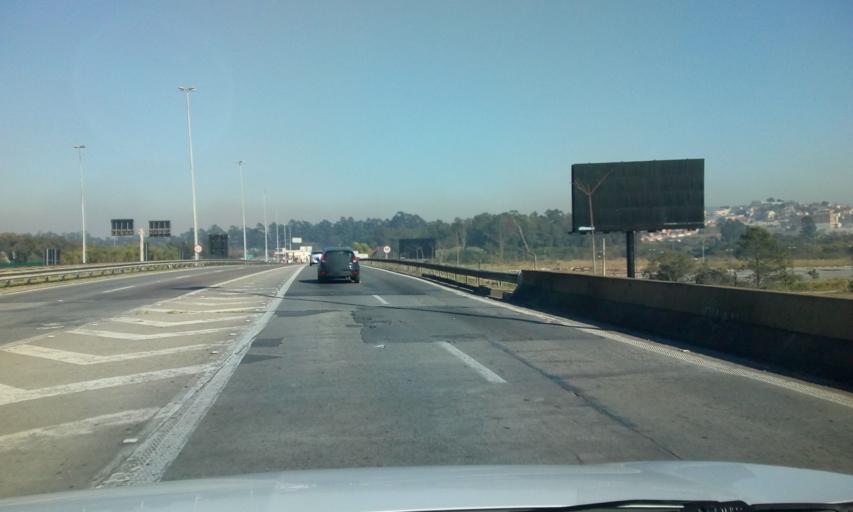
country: BR
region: Sao Paulo
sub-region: Guarulhos
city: Guarulhos
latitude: -23.4224
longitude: -46.4842
